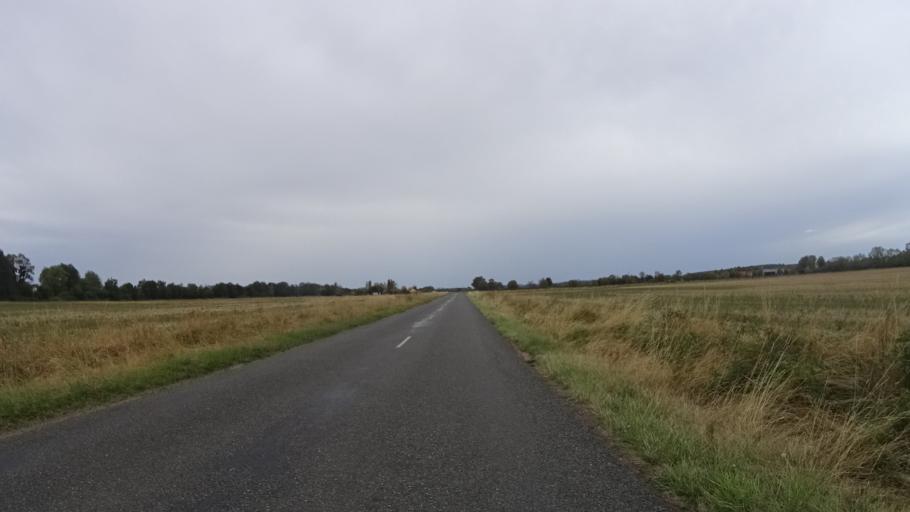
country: FR
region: Bourgogne
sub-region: Departement de la Nievre
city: Decize
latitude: 46.7835
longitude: 3.5326
